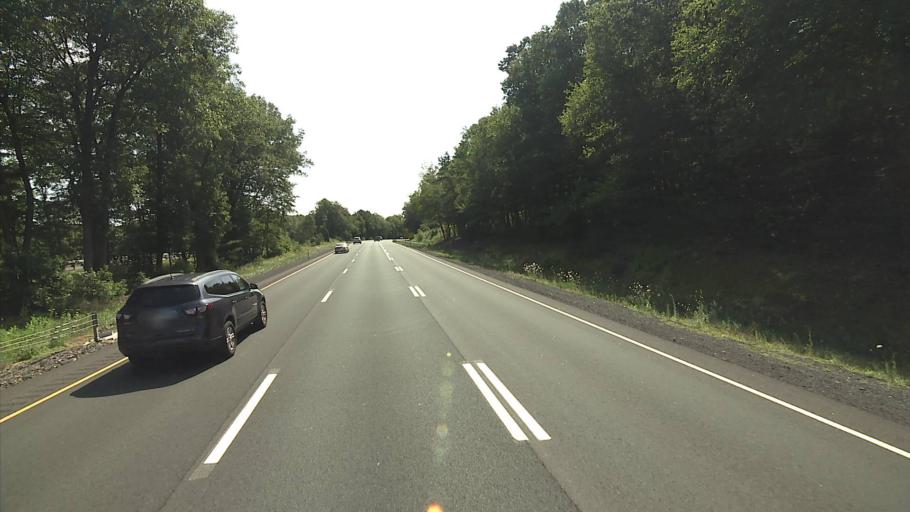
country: US
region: Connecticut
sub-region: Hartford County
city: Glastonbury Center
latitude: 41.6967
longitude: -72.5495
